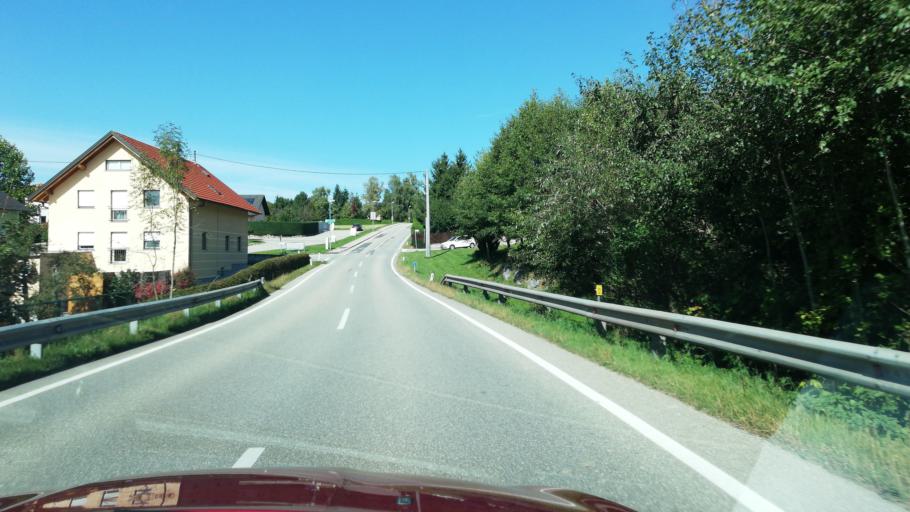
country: AT
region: Upper Austria
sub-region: Politischer Bezirk Vocklabruck
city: Zell am Pettenfirst
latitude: 48.1443
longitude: 13.5705
